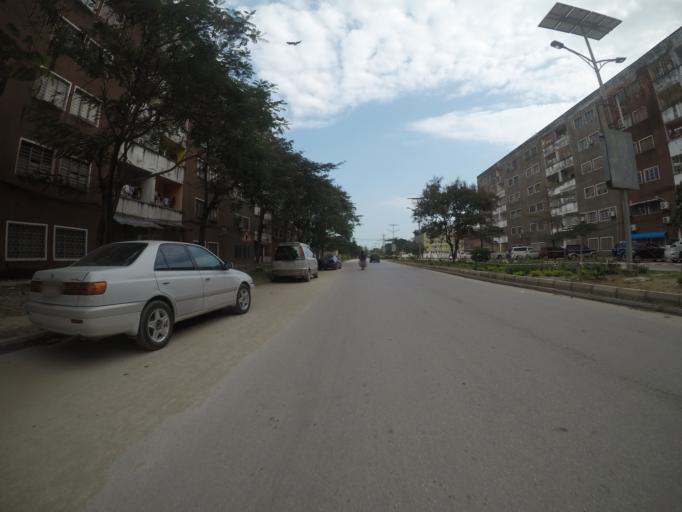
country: TZ
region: Zanzibar Urban/West
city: Zanzibar
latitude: -6.1698
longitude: 39.1988
